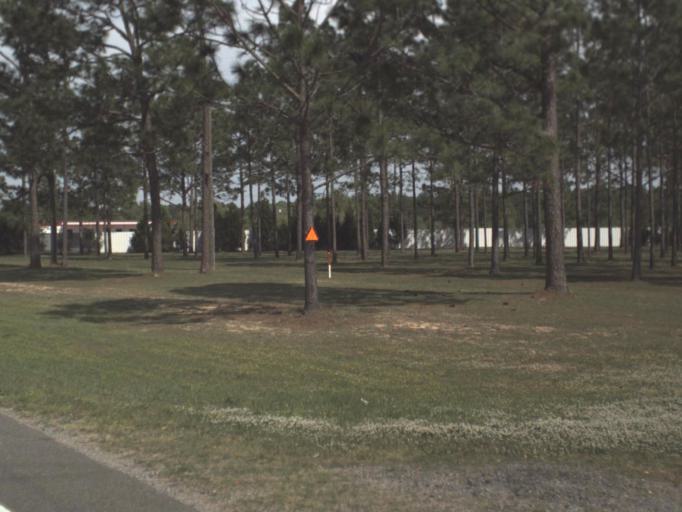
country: US
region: Florida
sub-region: Santa Rosa County
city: East Milton
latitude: 30.6765
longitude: -86.8516
